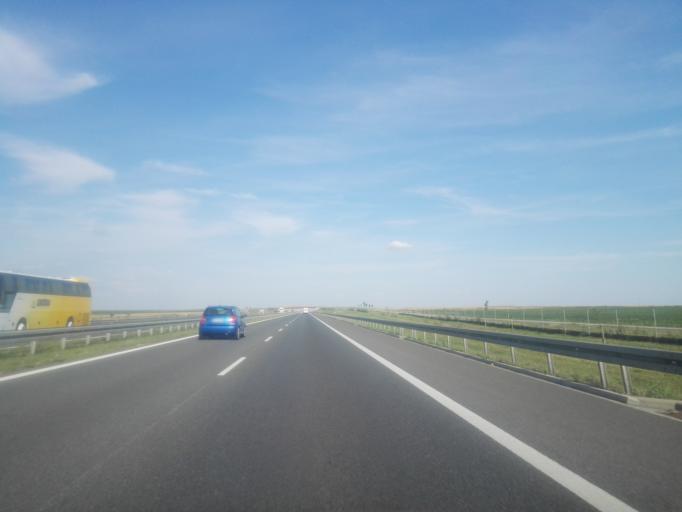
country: PL
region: Lower Silesian Voivodeship
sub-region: Powiat wroclawski
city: Dlugoleka
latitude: 51.2280
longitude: 17.2605
